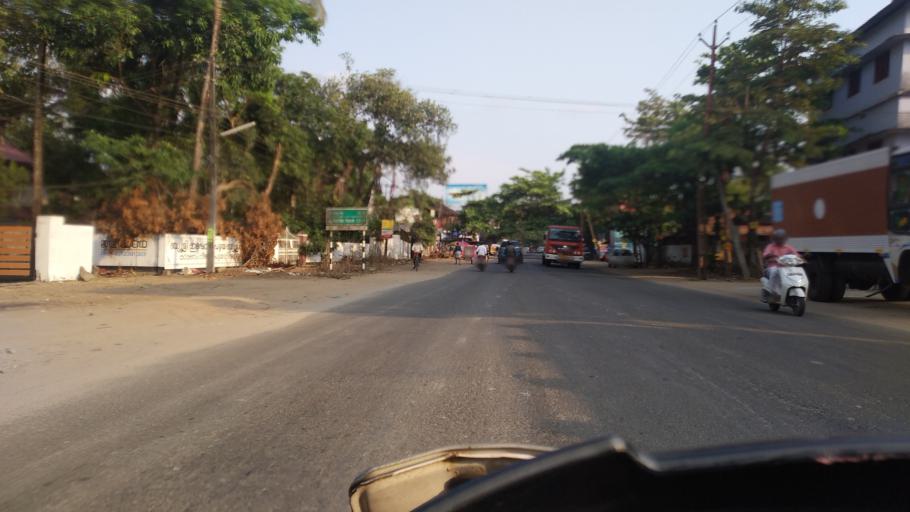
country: IN
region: Kerala
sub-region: Thrissur District
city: Thanniyam
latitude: 10.4216
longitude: 76.1043
